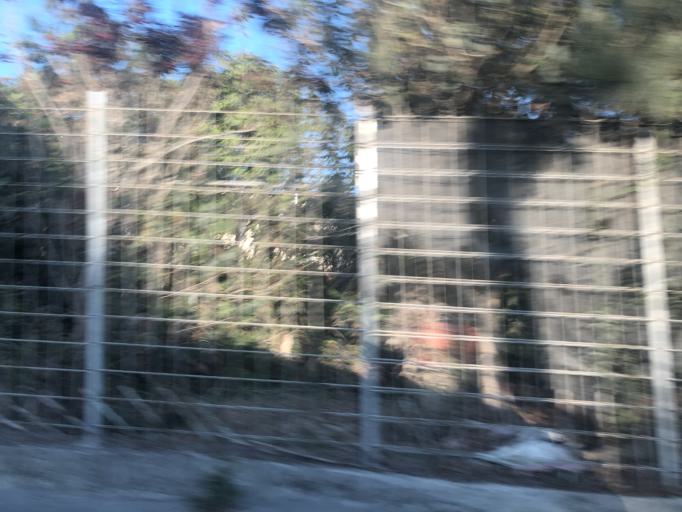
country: TW
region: Taiwan
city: Fengyuan
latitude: 24.2785
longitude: 120.7776
